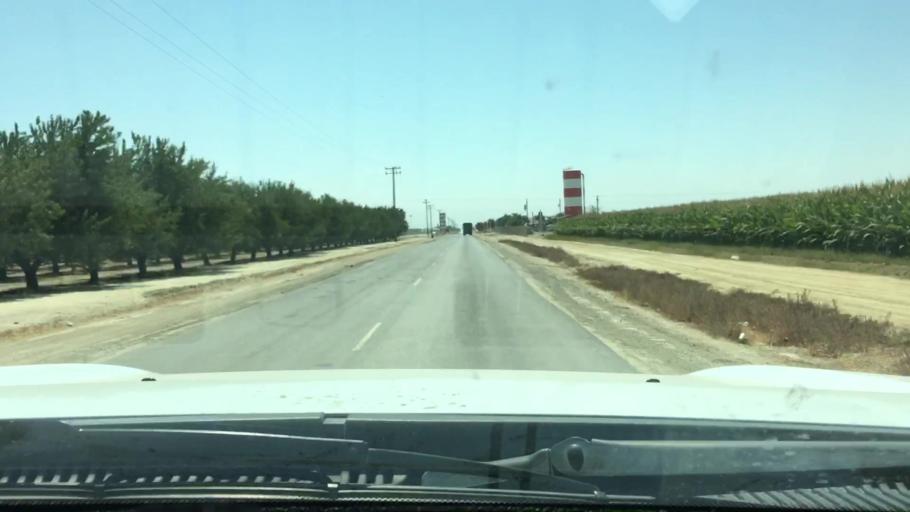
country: US
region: California
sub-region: Kern County
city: Wasco
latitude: 35.5671
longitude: -119.4028
